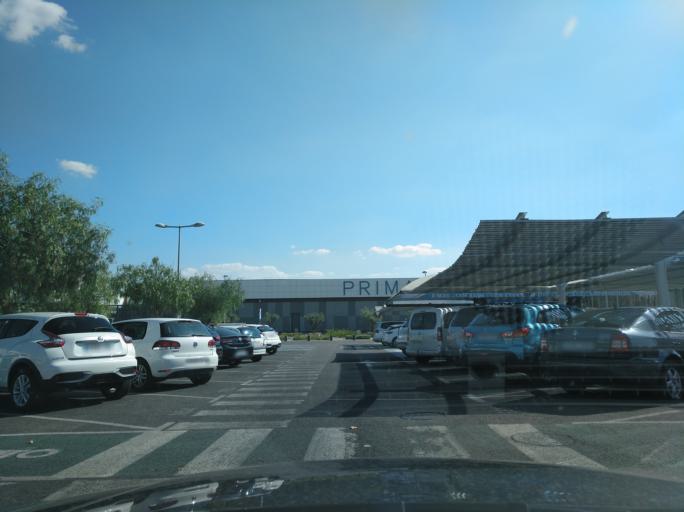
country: ES
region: Extremadura
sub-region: Provincia de Badajoz
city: Badajoz
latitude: 38.8853
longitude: -7.0213
